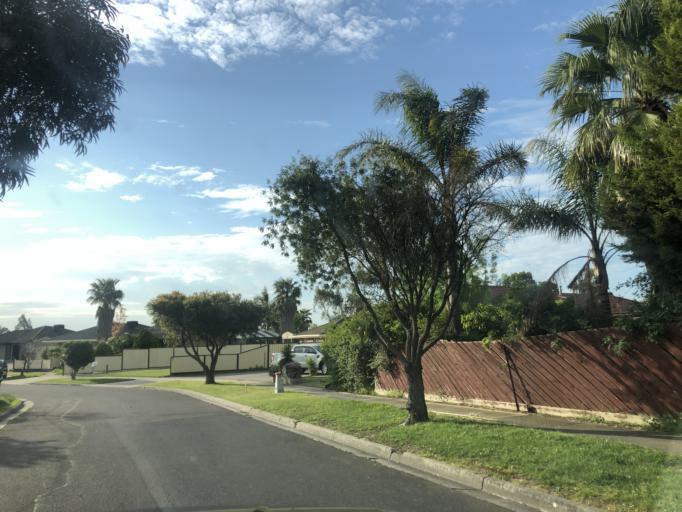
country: AU
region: Victoria
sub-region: Casey
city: Hallam
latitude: -38.0225
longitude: 145.2606
